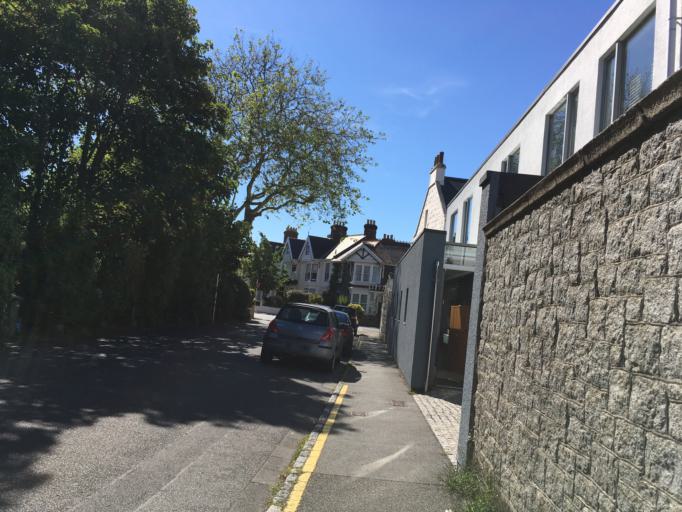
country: GG
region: St Peter Port
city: Saint Peter Port
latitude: 49.4587
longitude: -2.5438
